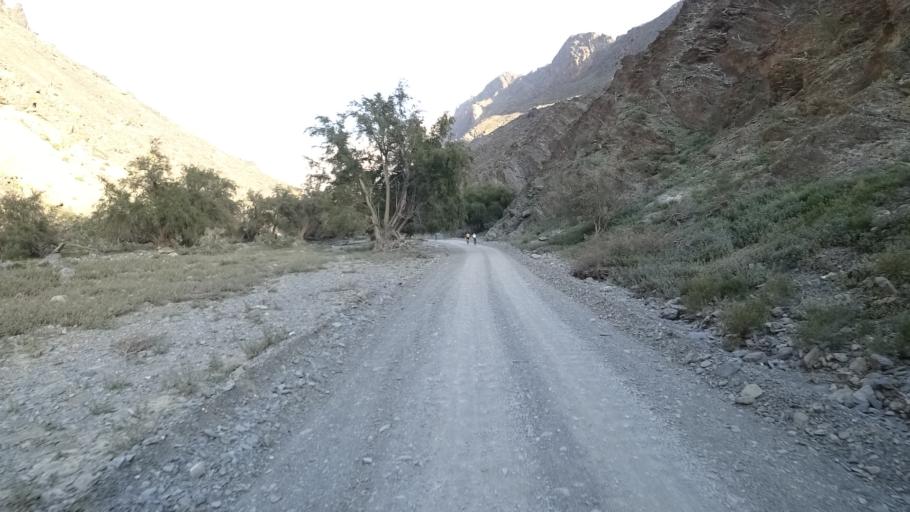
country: OM
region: Al Batinah
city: Bayt al `Awabi
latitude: 23.2547
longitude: 57.4027
